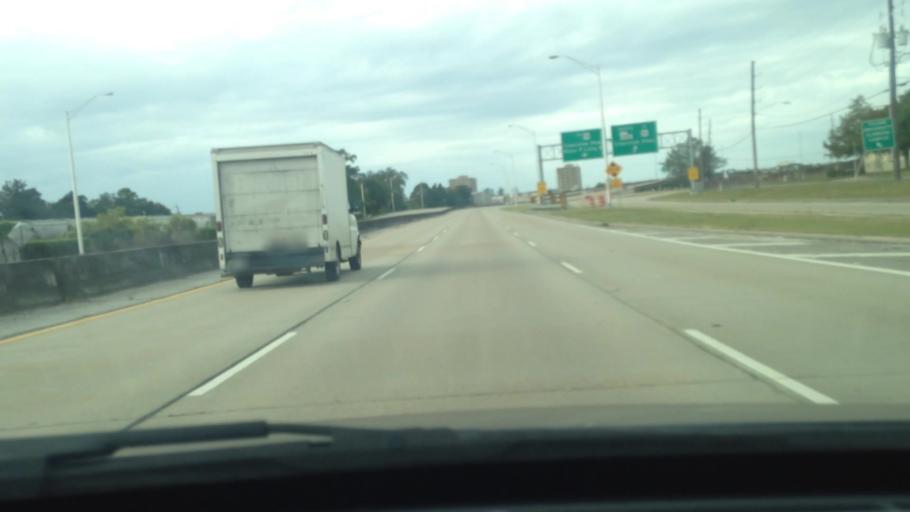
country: US
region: Louisiana
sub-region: Jefferson Parish
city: Metairie Terrace
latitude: 29.9701
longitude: -90.1774
